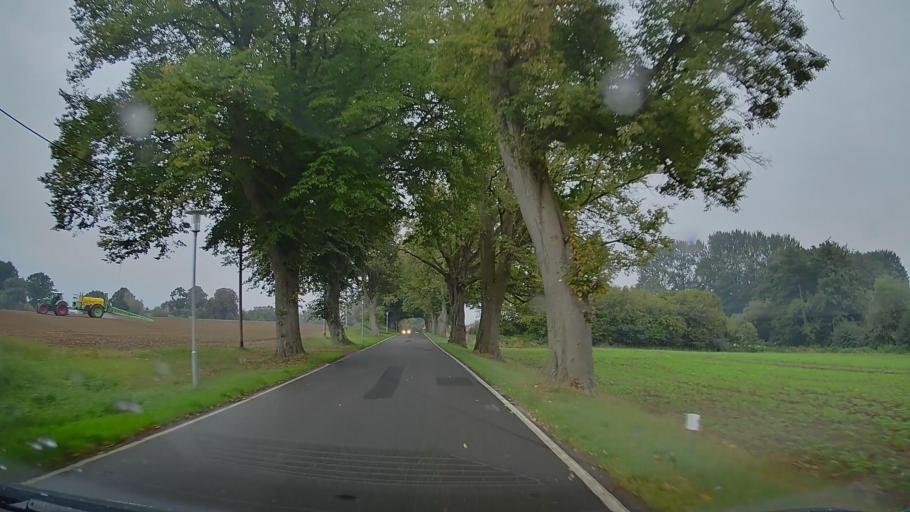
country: DE
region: Mecklenburg-Vorpommern
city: Kalkhorst
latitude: 53.9965
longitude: 11.0994
